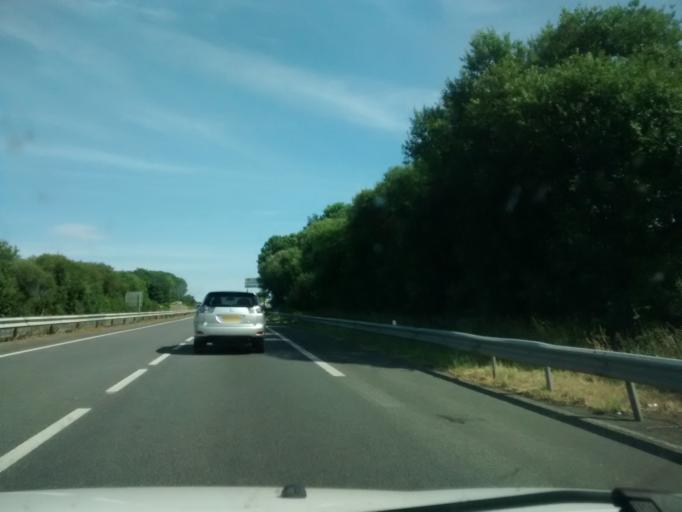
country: FR
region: Brittany
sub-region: Departement des Cotes-d'Armor
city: Plenee-Jugon
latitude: 48.3958
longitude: -2.4020
